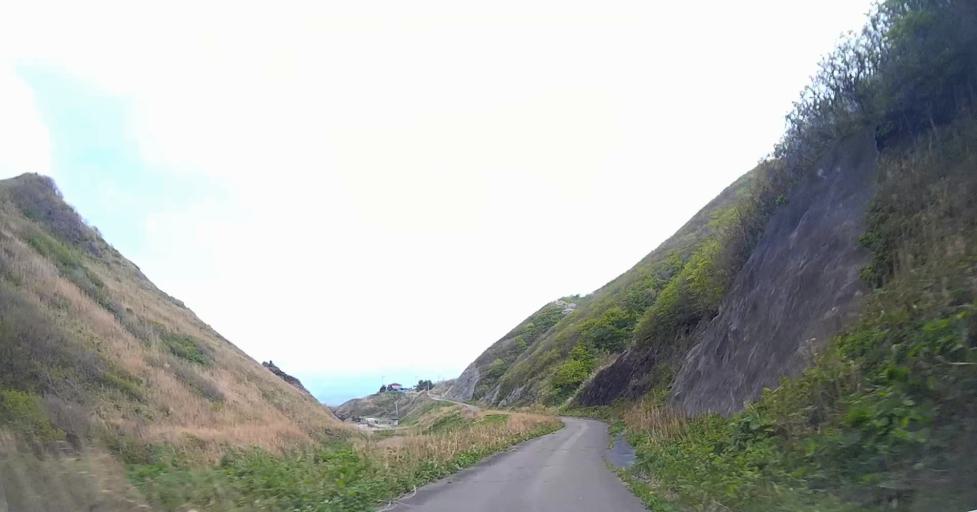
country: JP
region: Aomori
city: Shimokizukuri
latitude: 41.2402
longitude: 140.3435
